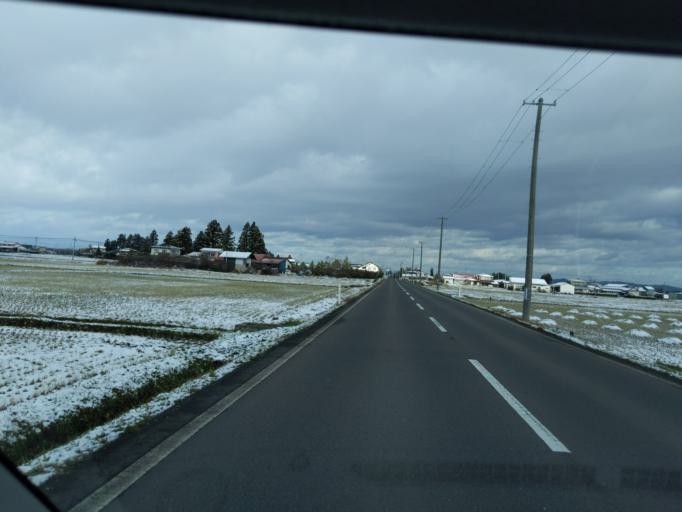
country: JP
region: Iwate
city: Mizusawa
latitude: 39.1592
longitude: 141.1118
